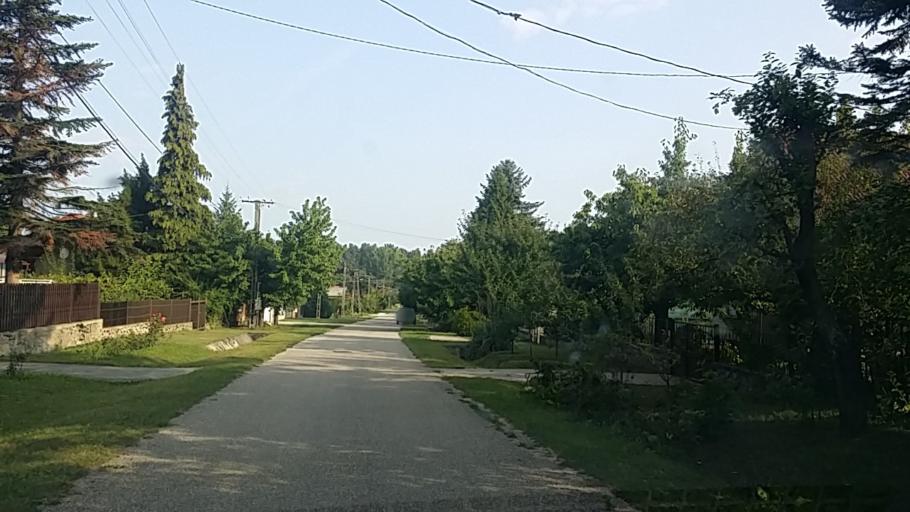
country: HU
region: Gyor-Moson-Sopron
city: Nagycenk
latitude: 47.6178
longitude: 16.7797
